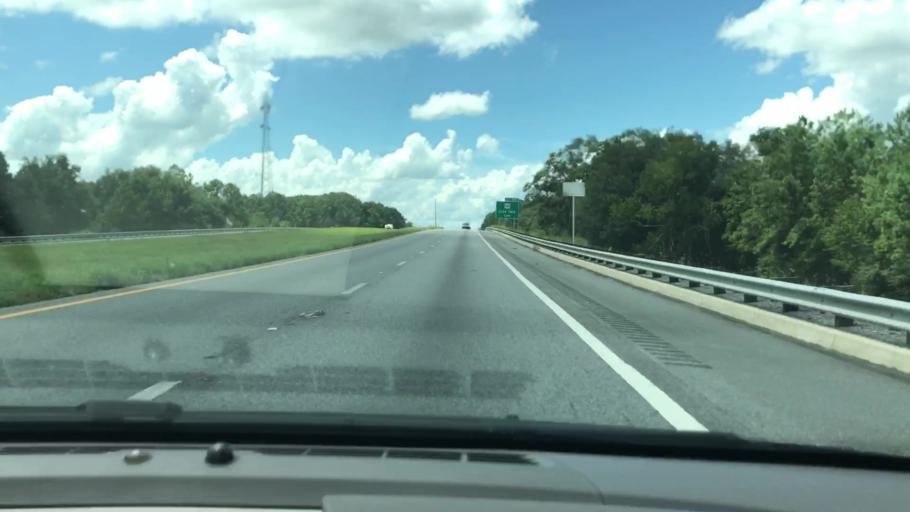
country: US
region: Florida
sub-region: Suwannee County
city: Live Oak
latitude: 30.3451
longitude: -83.0862
